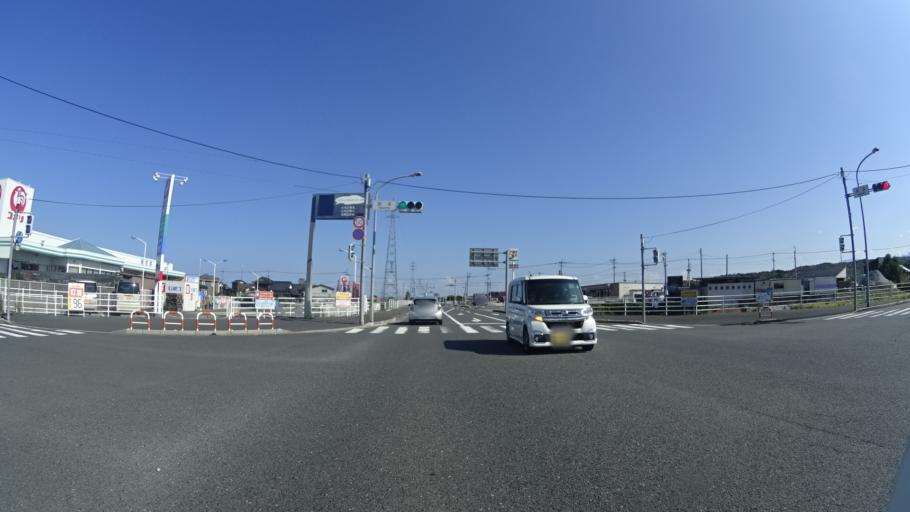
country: JP
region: Fukuoka
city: Shiida
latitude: 33.6514
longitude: 131.0507
